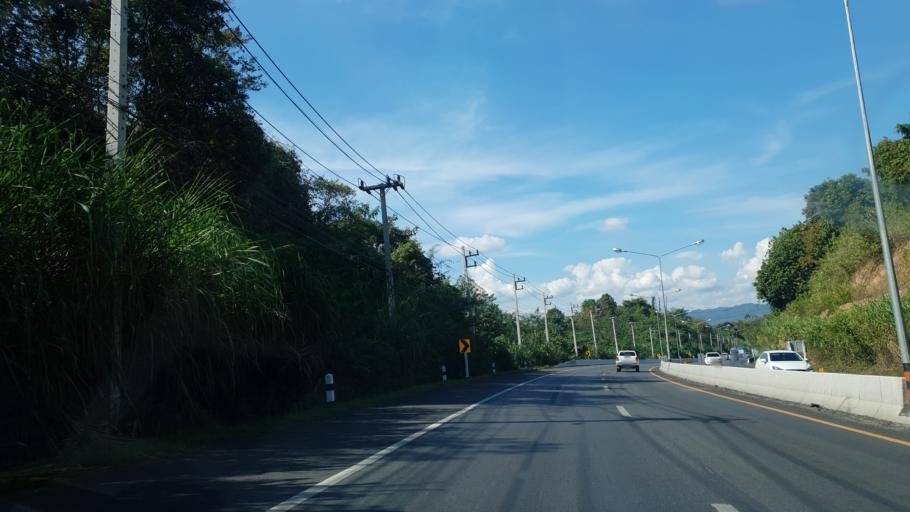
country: TH
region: Phrae
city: Den Chai
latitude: 17.8388
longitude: 100.0541
